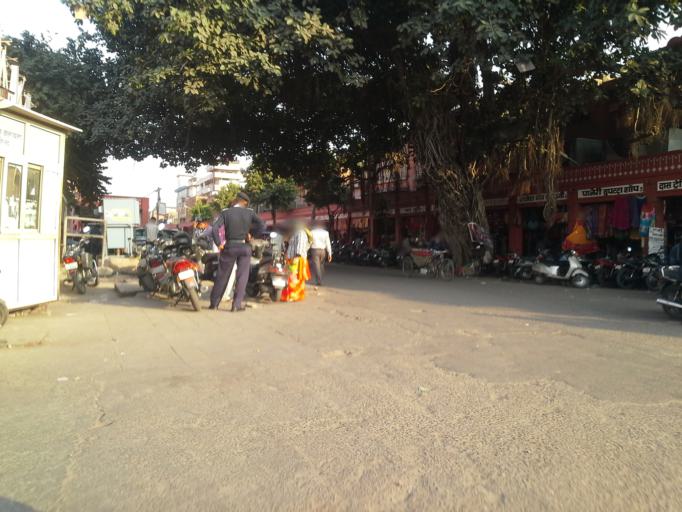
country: IN
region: Rajasthan
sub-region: Jaipur
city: Jaipur
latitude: 26.9170
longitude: 75.8209
